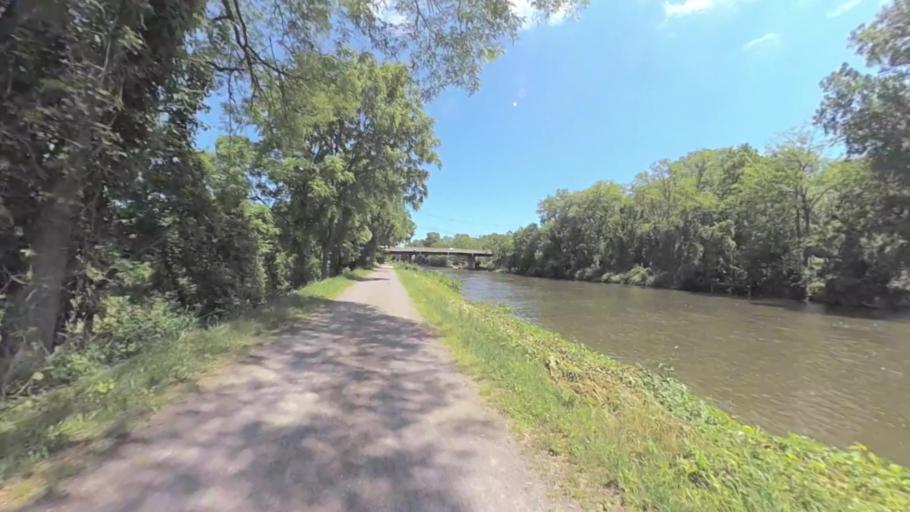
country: US
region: New York
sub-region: Monroe County
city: Fairport
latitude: 43.0783
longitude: -77.4616
